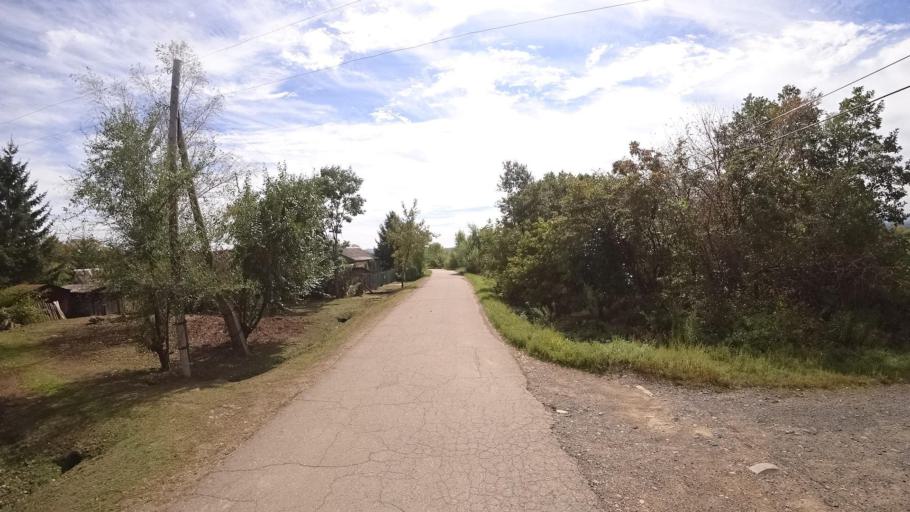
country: RU
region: Primorskiy
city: Yakovlevka
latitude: 44.6463
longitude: 133.5920
